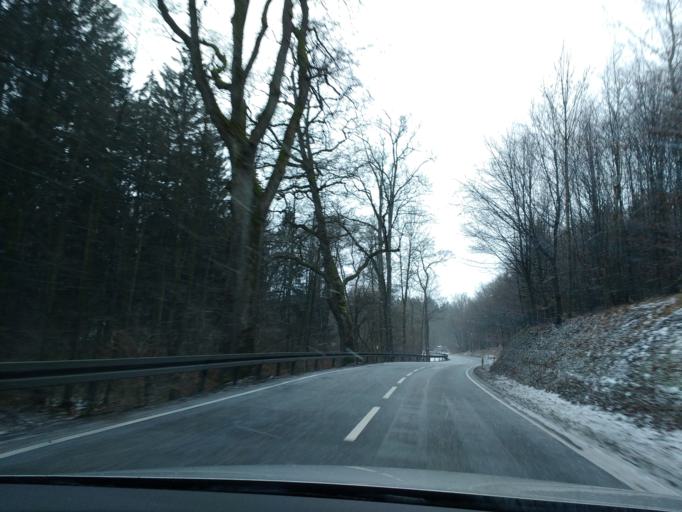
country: DE
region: North Rhine-Westphalia
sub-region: Regierungsbezirk Arnsberg
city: Brilon
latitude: 51.4519
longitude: 8.5998
